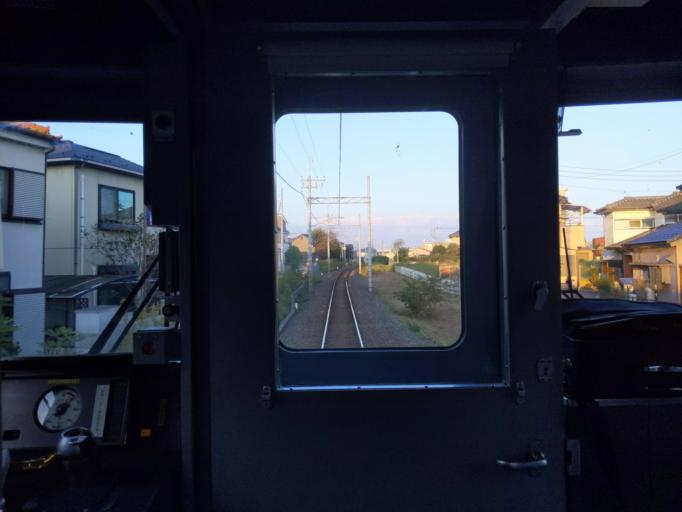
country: JP
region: Saitama
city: Kasukabe
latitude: 35.9771
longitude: 139.7685
